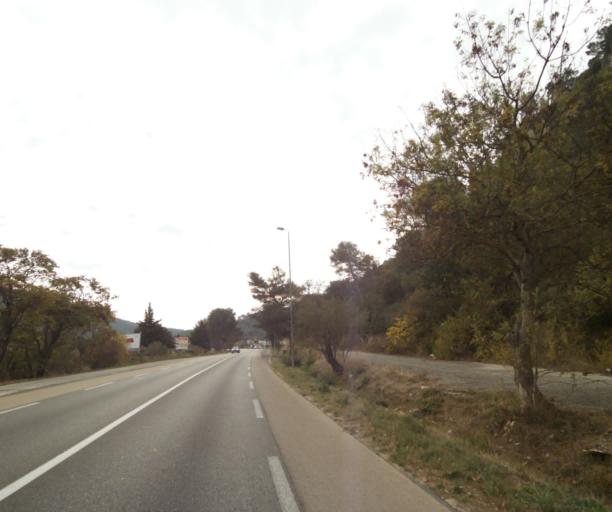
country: FR
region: Provence-Alpes-Cote d'Azur
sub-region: Departement des Bouches-du-Rhone
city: Gemenos
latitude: 43.2761
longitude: 5.6313
